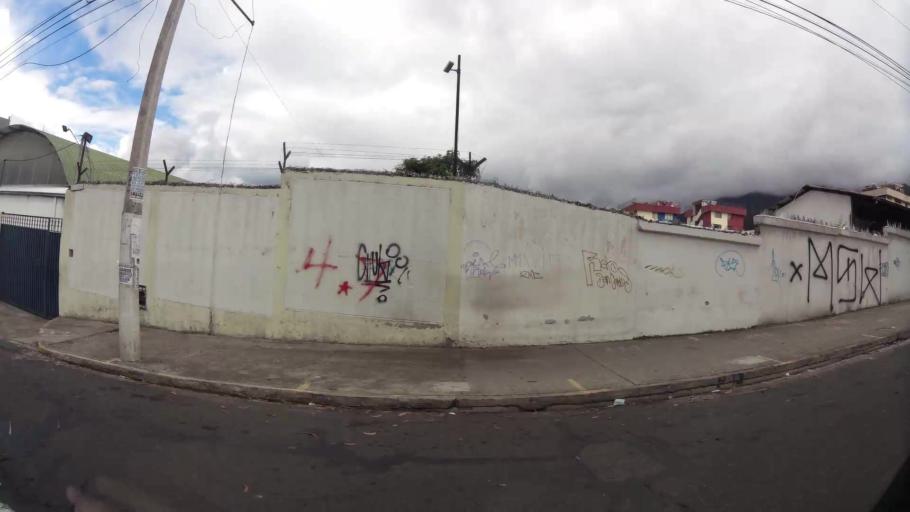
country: EC
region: Pichincha
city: Quito
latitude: -0.1337
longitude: -78.4996
